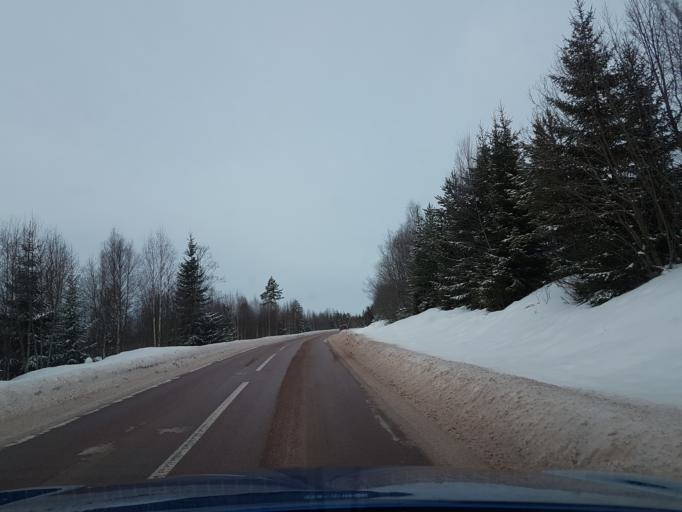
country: SE
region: Dalarna
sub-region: Orsa Kommun
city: Orsa
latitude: 61.2267
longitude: 14.7006
